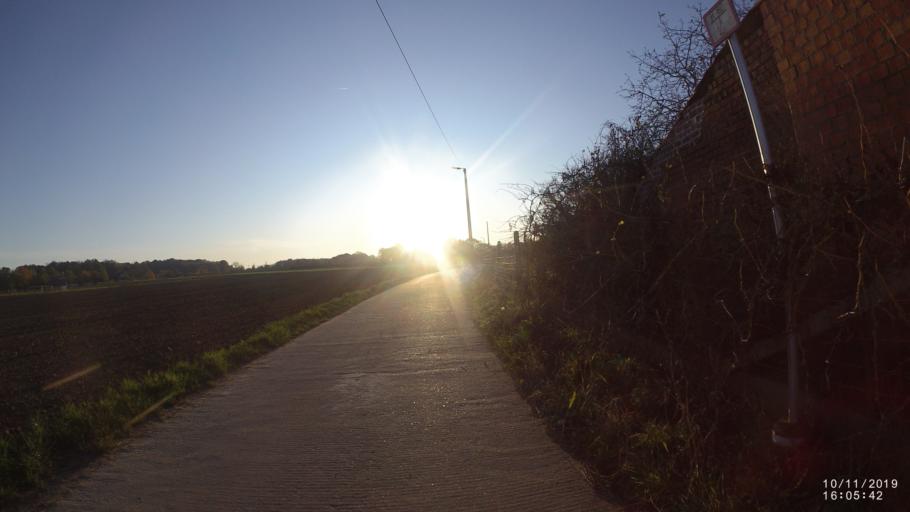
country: BE
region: Flanders
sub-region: Provincie Vlaams-Brabant
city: Lubbeek
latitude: 50.9014
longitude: 4.8585
